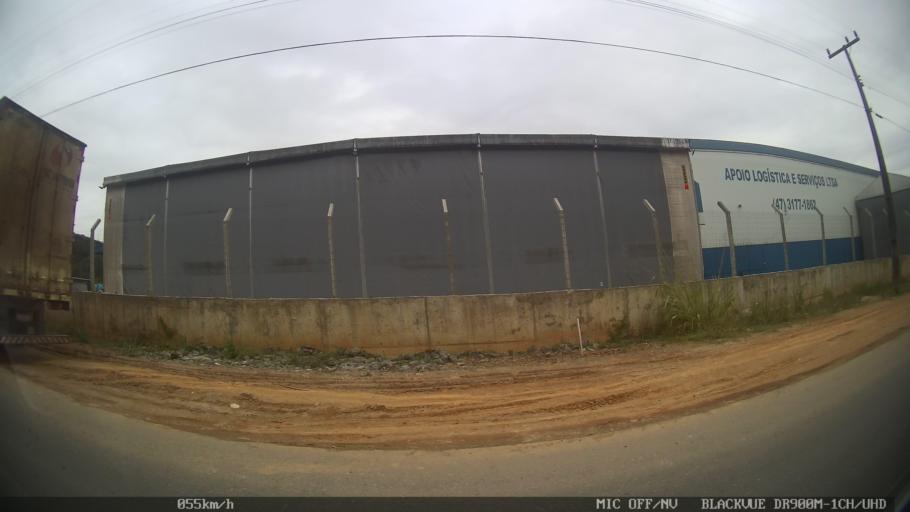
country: BR
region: Santa Catarina
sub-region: Joinville
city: Joinville
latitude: -26.2575
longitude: -48.8993
